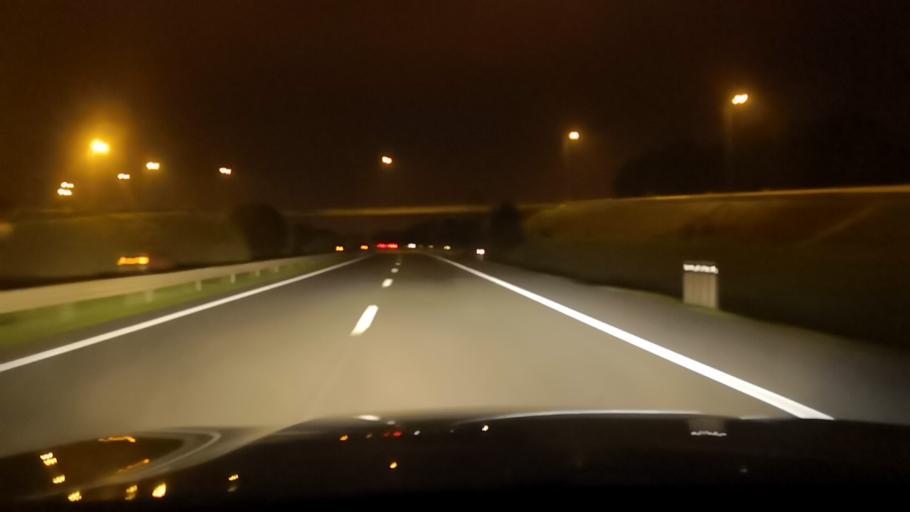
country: PT
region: Setubal
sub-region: Palmela
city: Palmela
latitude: 38.5581
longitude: -8.8691
